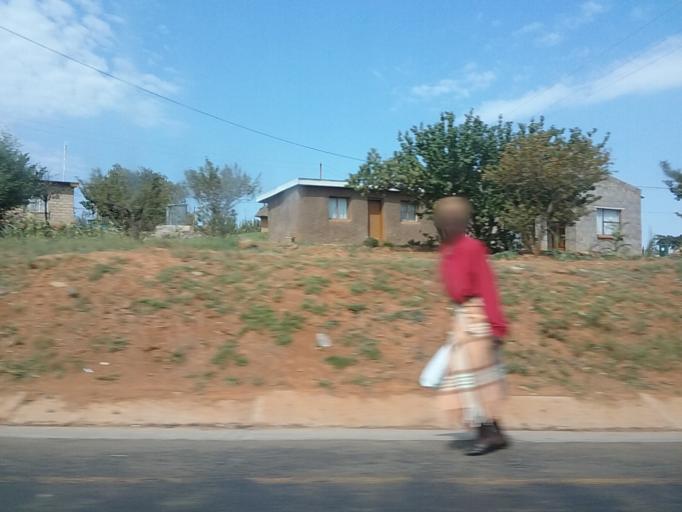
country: LS
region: Berea
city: Teyateyaneng
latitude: -29.1173
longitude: 27.9736
